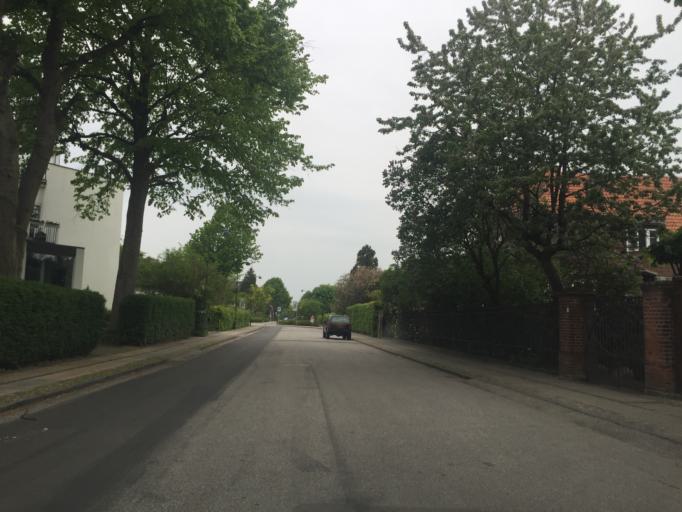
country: DK
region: Capital Region
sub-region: Gentofte Kommune
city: Charlottenlund
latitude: 55.7349
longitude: 12.5644
